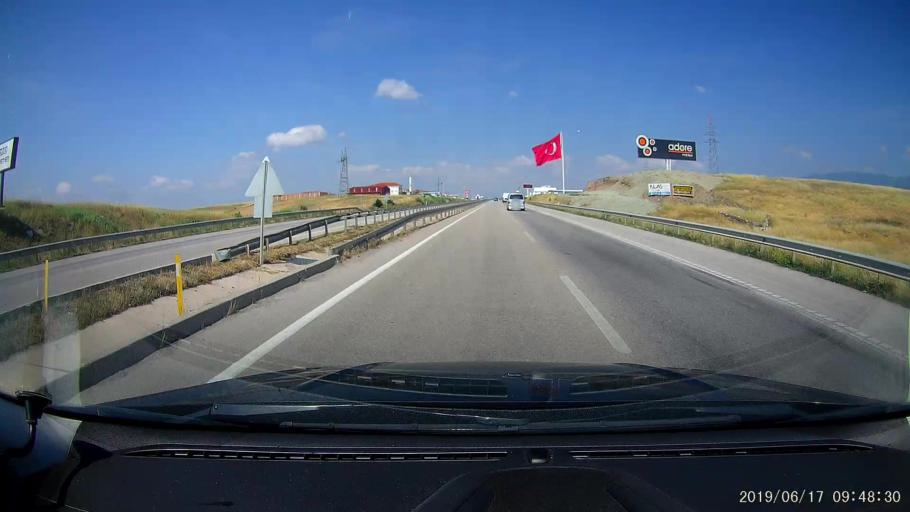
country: TR
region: Amasya
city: Merzifon
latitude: 40.8745
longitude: 35.5513
